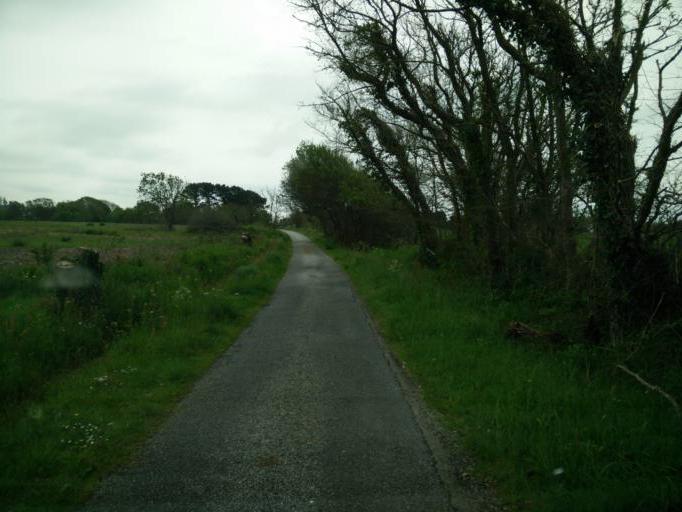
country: FR
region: Brittany
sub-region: Departement du Finistere
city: Tregunc
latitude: 47.8261
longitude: -3.8789
